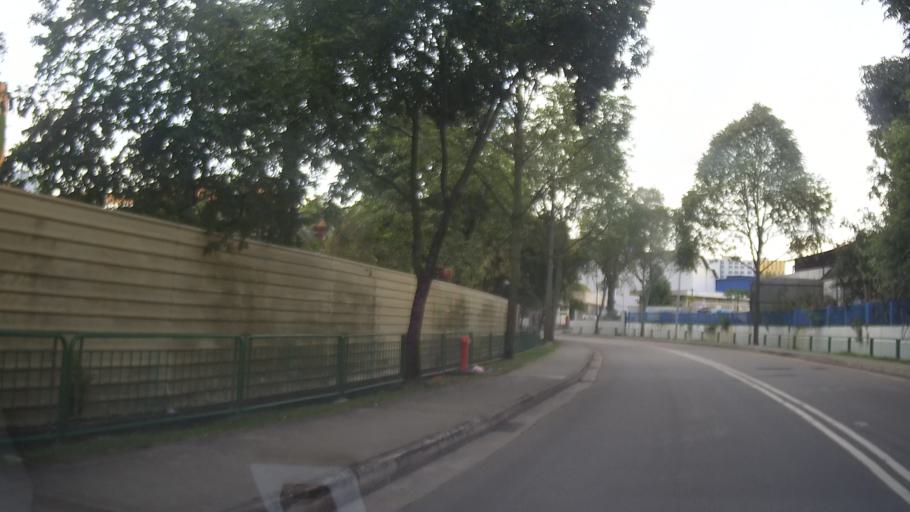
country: MY
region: Johor
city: Johor Bahru
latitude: 1.4194
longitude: 103.7447
